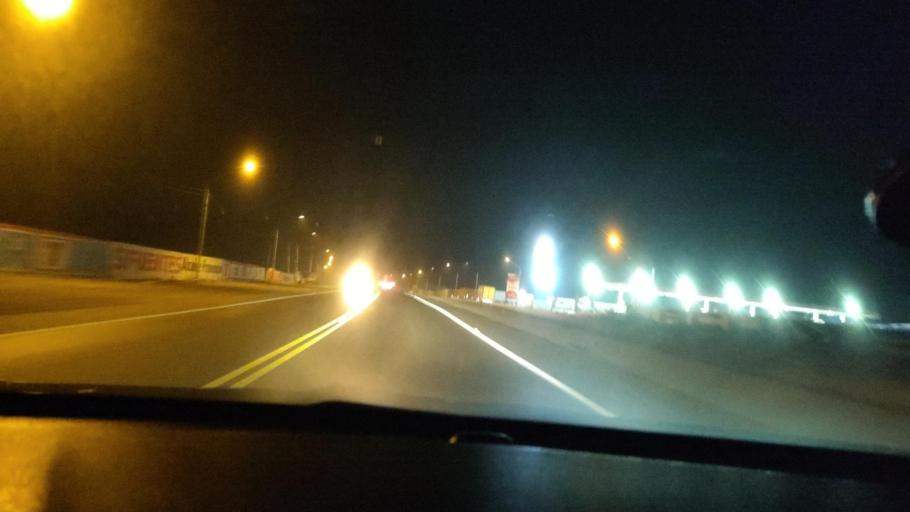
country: PE
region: La Libertad
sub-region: Provincia de Trujillo
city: Huanchaco
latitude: -8.1012
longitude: -79.0991
